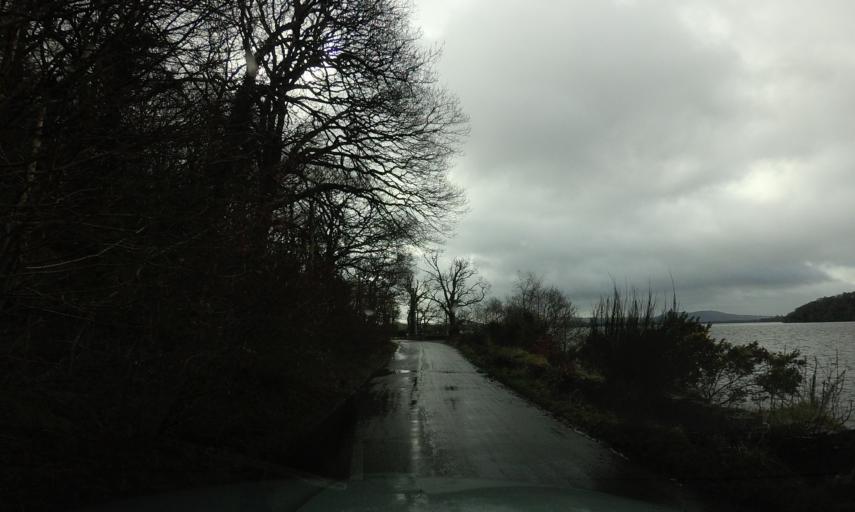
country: GB
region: Scotland
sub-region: West Dunbartonshire
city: Balloch
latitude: 56.1152
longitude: -4.5857
